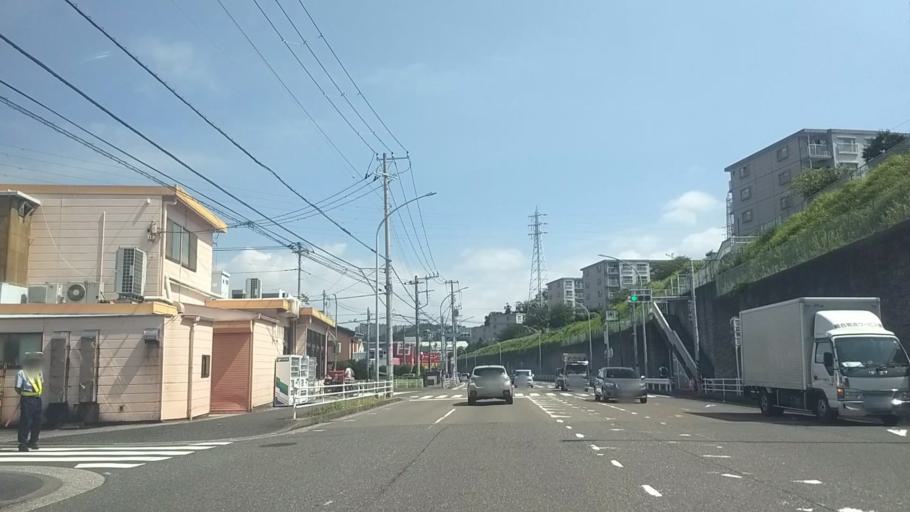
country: JP
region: Kanagawa
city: Zushi
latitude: 35.3384
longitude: 139.6102
